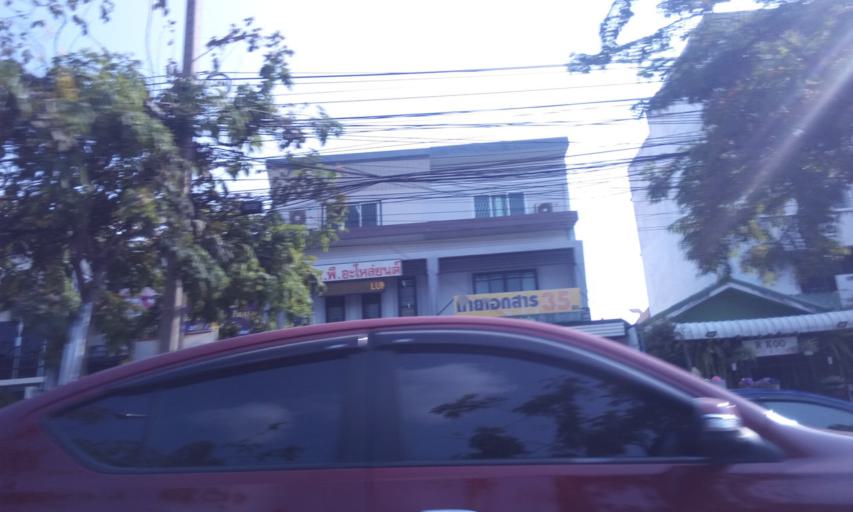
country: TH
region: Bangkok
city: Don Mueang
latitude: 13.9260
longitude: 100.5902
